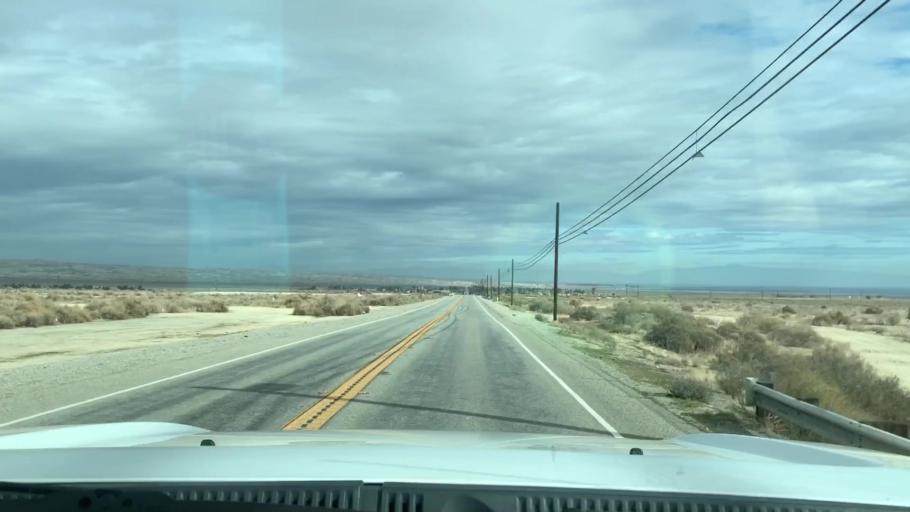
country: US
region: California
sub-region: Kern County
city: Ford City
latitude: 35.1892
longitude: -119.4356
